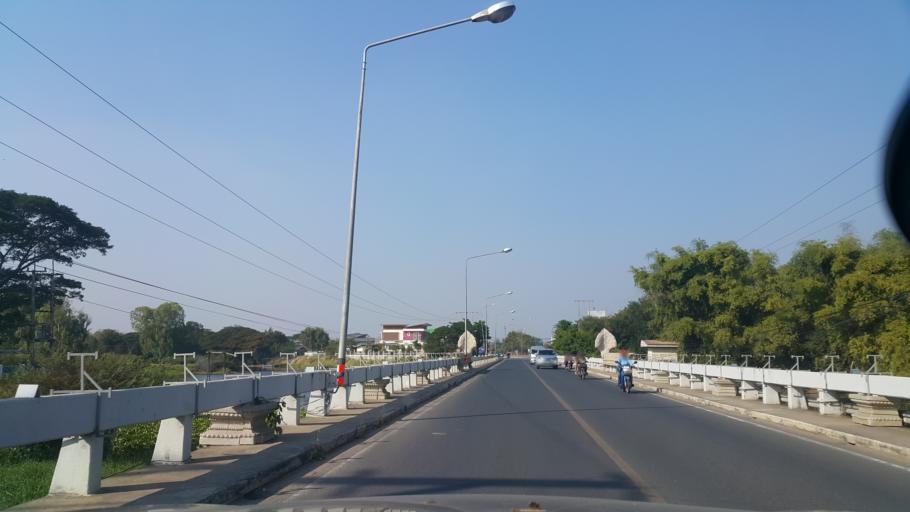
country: TH
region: Nakhon Ratchasima
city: Phimai
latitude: 15.2249
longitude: 102.4940
